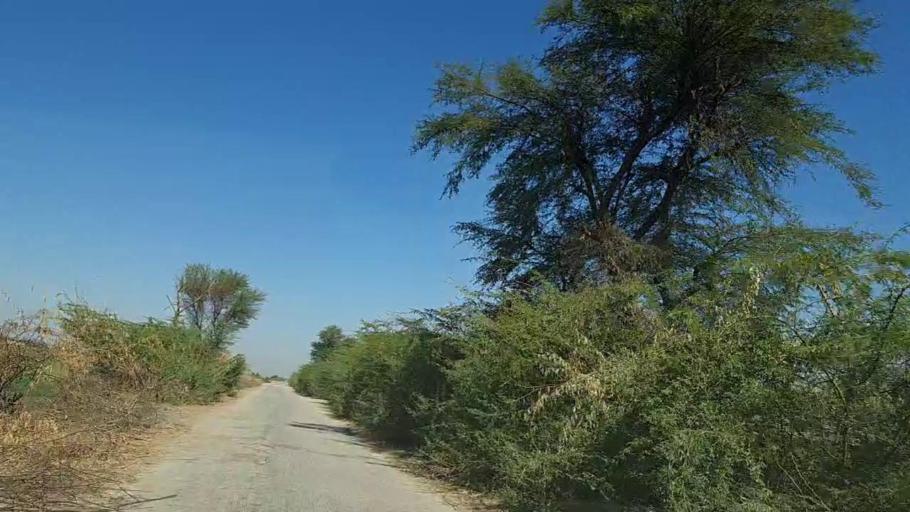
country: PK
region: Sindh
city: Dhoro Naro
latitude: 25.4705
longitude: 69.5262
